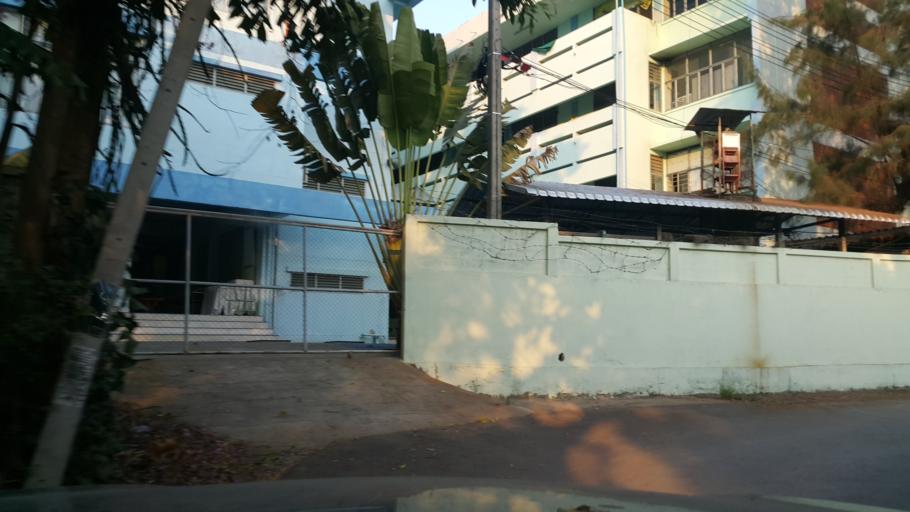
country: TH
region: Chiang Mai
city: Saraphi
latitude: 18.7253
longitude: 99.0234
